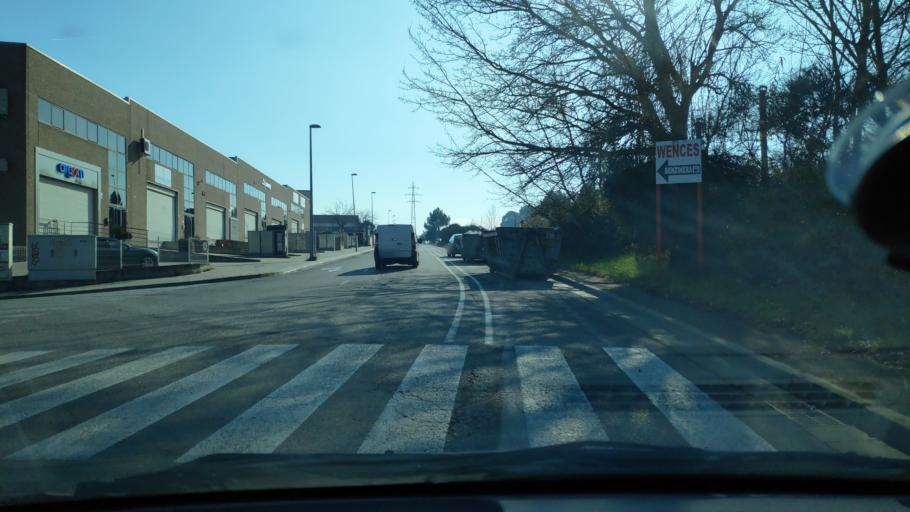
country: ES
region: Catalonia
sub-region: Provincia de Barcelona
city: Sant Quirze del Valles
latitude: 41.5241
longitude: 2.0887
